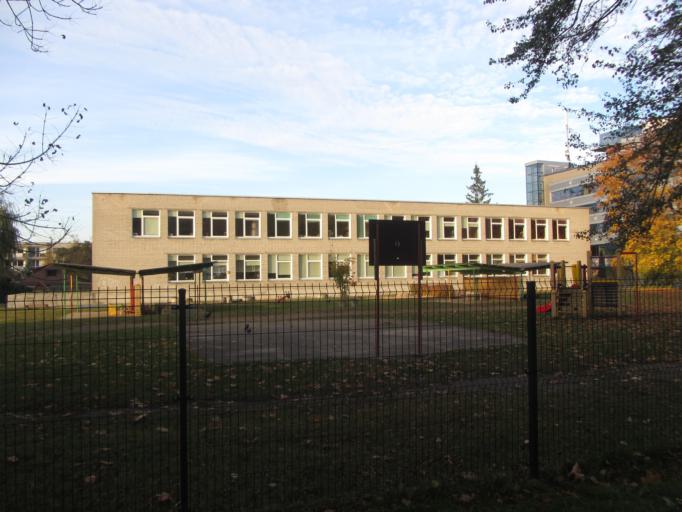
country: LT
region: Vilnius County
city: Naujamiestis
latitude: 54.6772
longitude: 25.2614
